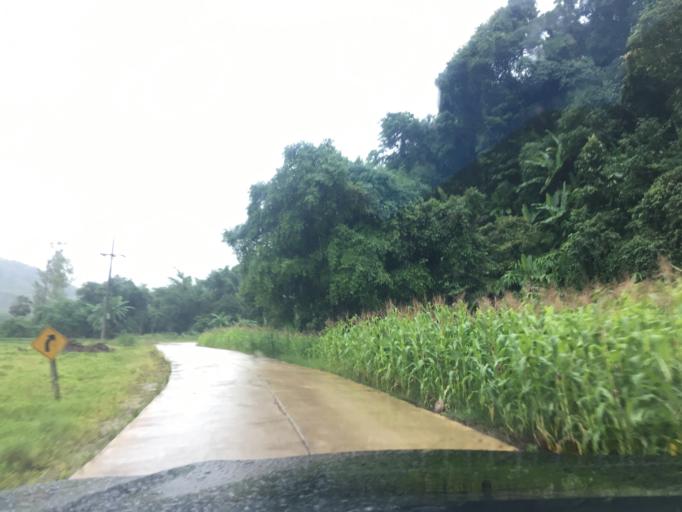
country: TH
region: Chiang Rai
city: Chiang Khong
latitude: 20.2967
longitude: 100.2569
